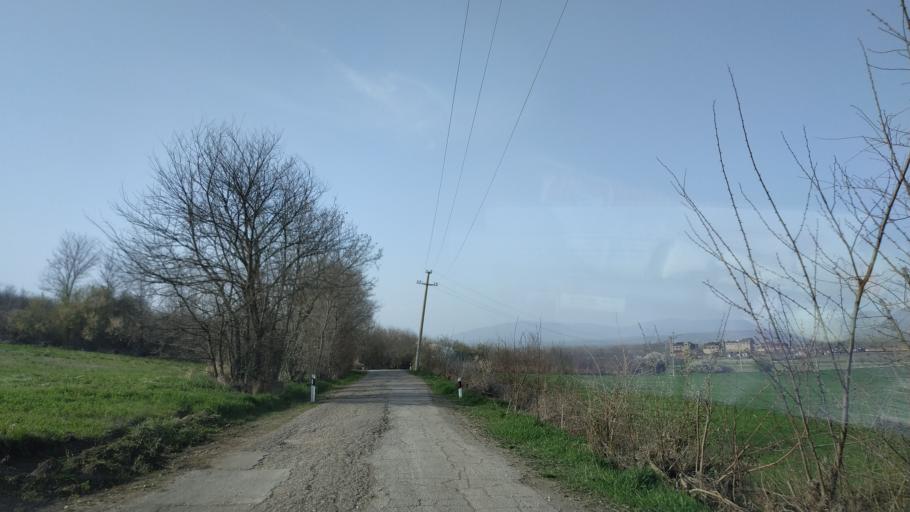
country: RS
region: Central Serbia
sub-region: Nisavski Okrug
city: Aleksinac
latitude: 43.5155
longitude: 21.6478
